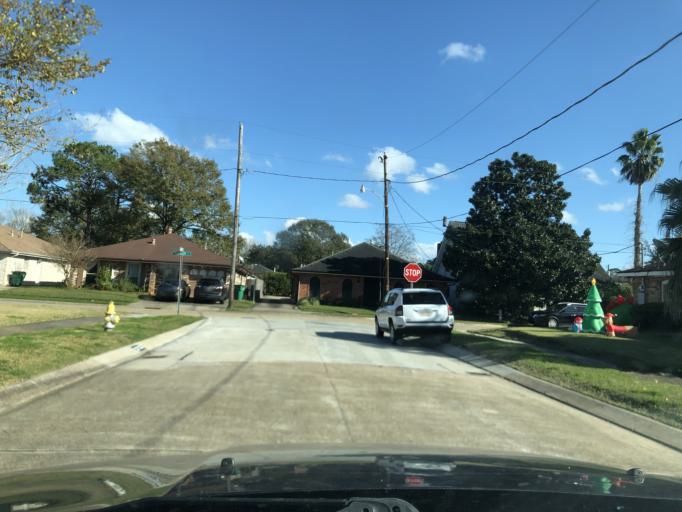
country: US
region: Louisiana
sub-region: Jefferson Parish
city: Metairie Terrace
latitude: 29.9869
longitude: -90.1648
